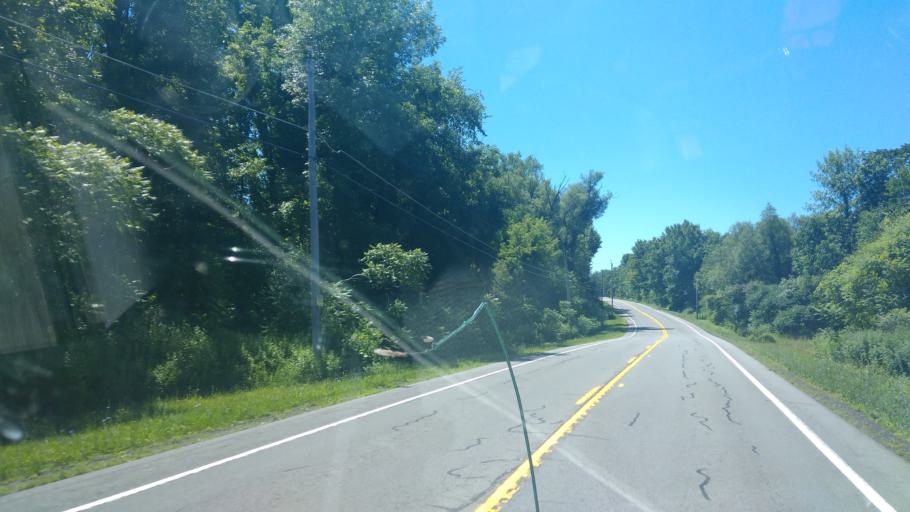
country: US
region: New York
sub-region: Wayne County
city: Sodus
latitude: 43.1743
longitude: -76.9877
